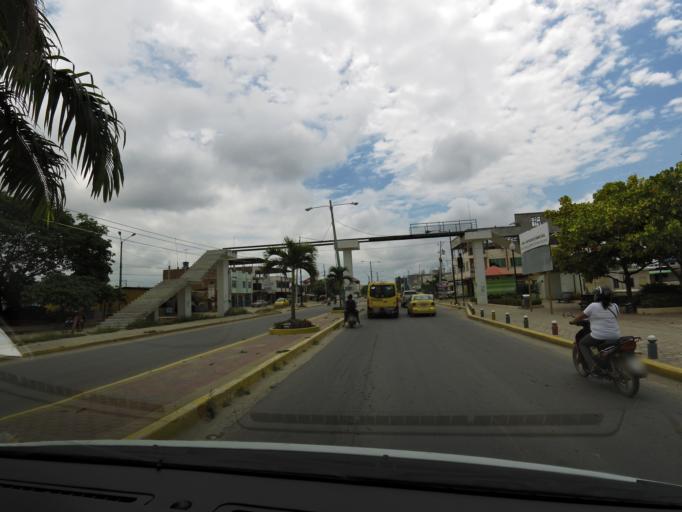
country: EC
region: El Oro
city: Huaquillas
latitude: -3.4832
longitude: -80.2216
